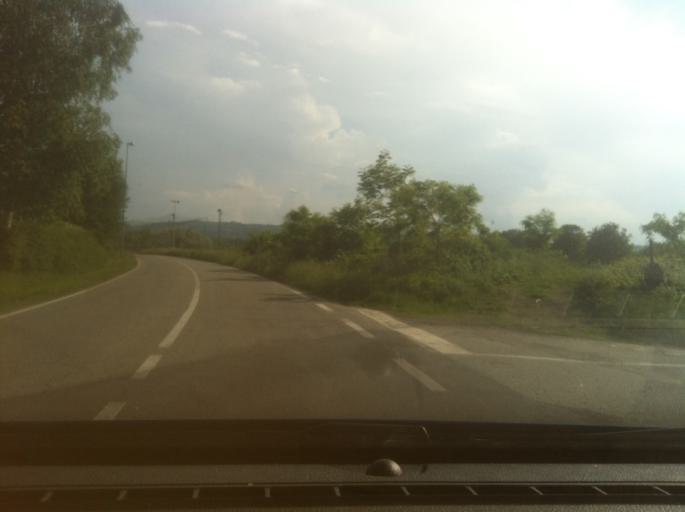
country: IT
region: Piedmont
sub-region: Provincia di Torino
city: Pavone Canavese
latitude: 45.4375
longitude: 7.8487
